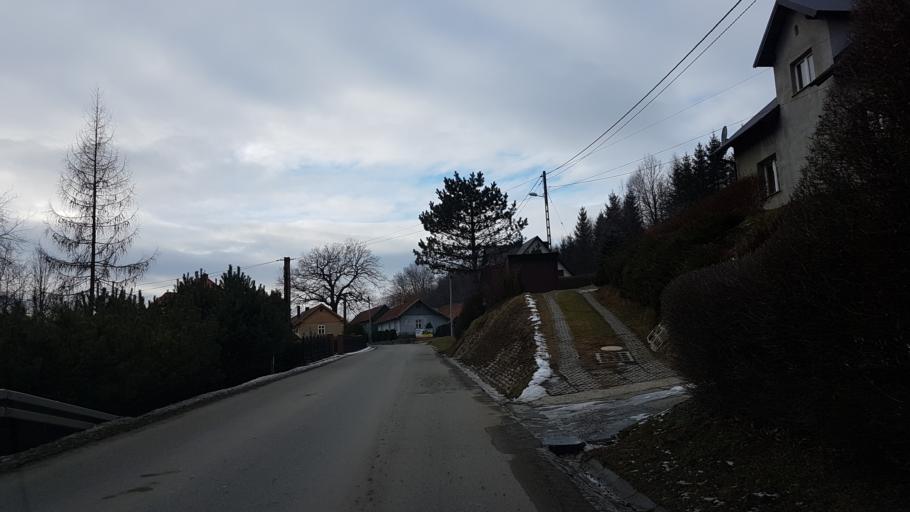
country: PL
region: Lesser Poland Voivodeship
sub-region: Powiat nowosadecki
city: Rytro
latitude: 49.5157
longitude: 20.6432
